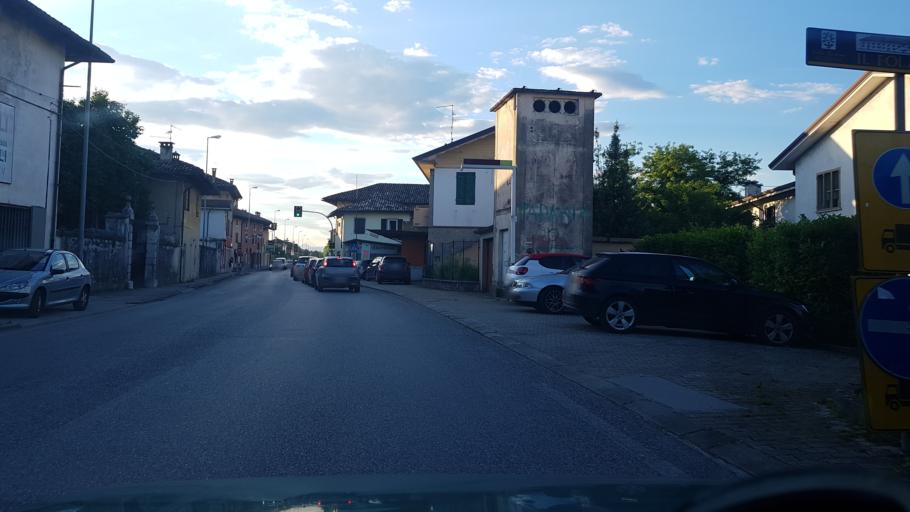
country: IT
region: Friuli Venezia Giulia
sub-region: Provincia di Udine
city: Santa Maria la Longa
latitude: 45.9325
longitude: 13.2919
